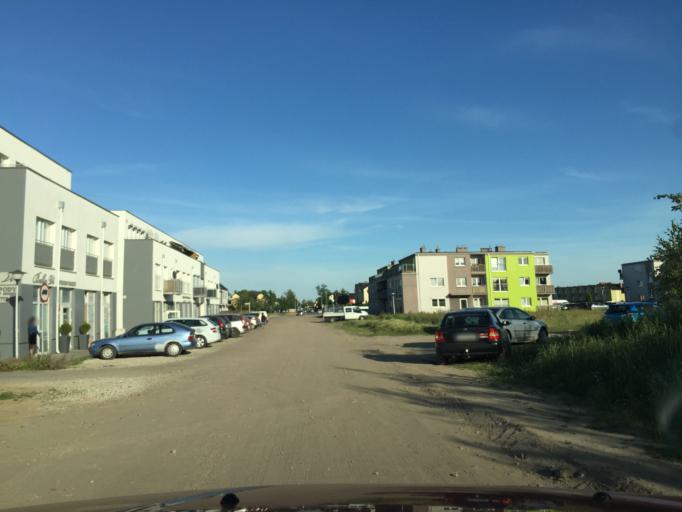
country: PL
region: Greater Poland Voivodeship
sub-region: Powiat poznanski
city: Plewiska
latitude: 52.3757
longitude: 16.8087
